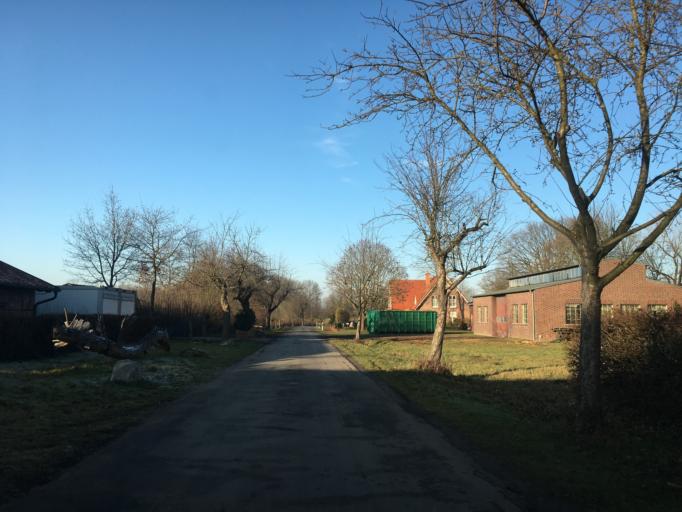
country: DE
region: North Rhine-Westphalia
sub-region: Regierungsbezirk Munster
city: Altenberge
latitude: 52.0359
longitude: 7.5240
